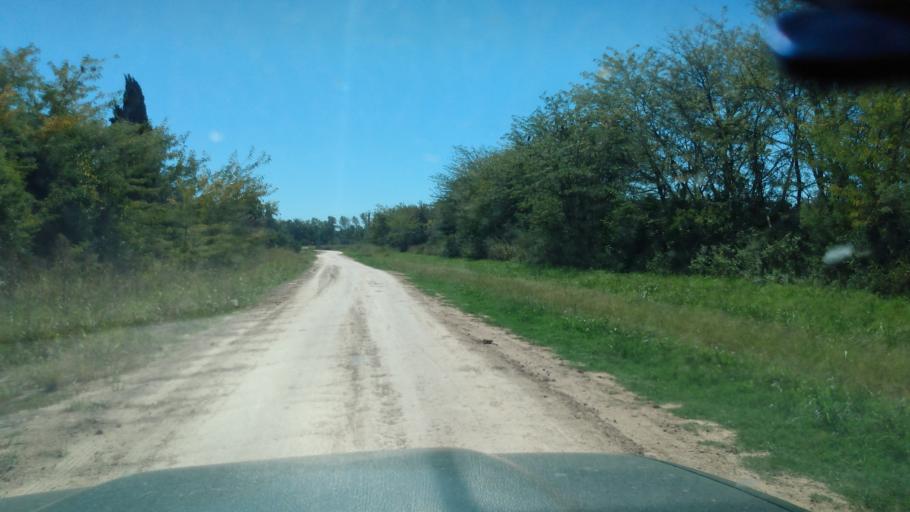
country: AR
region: Buenos Aires
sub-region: Partido de Lujan
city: Lujan
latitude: -34.5510
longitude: -59.1464
